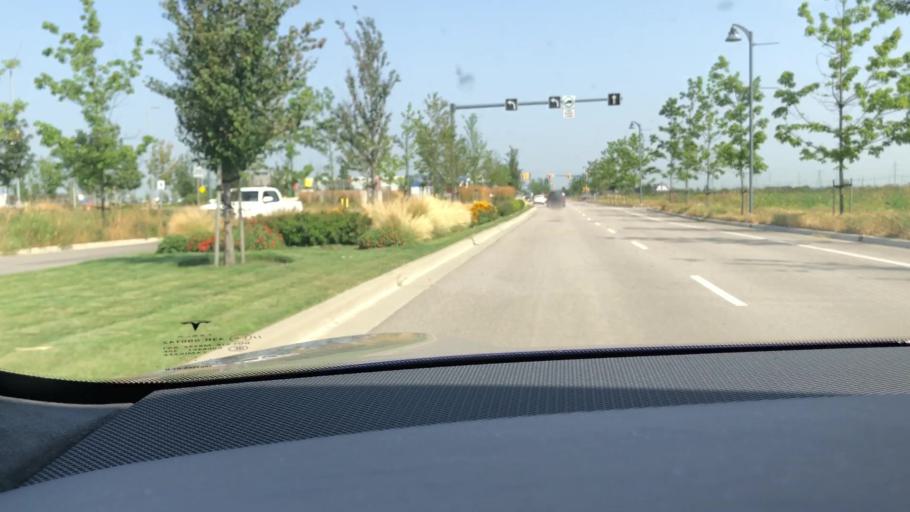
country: CA
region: British Columbia
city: Ladner
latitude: 49.0395
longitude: -123.0798
